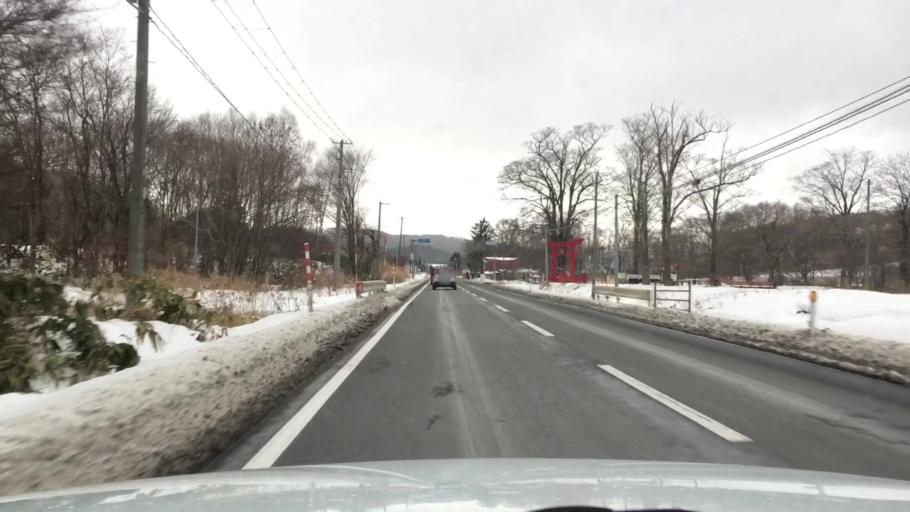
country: JP
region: Iwate
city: Morioka-shi
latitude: 39.6446
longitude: 141.3703
